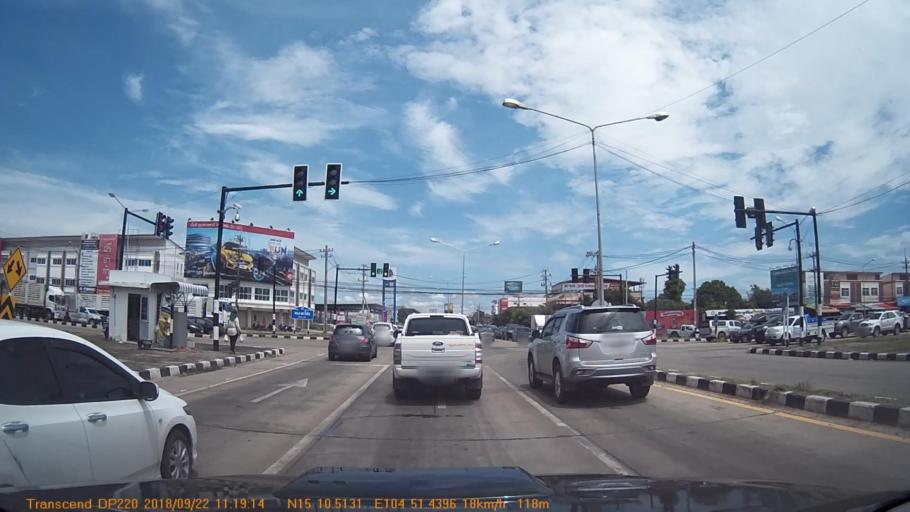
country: TH
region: Changwat Ubon Ratchathani
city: Warin Chamrap
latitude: 15.1752
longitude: 104.8573
